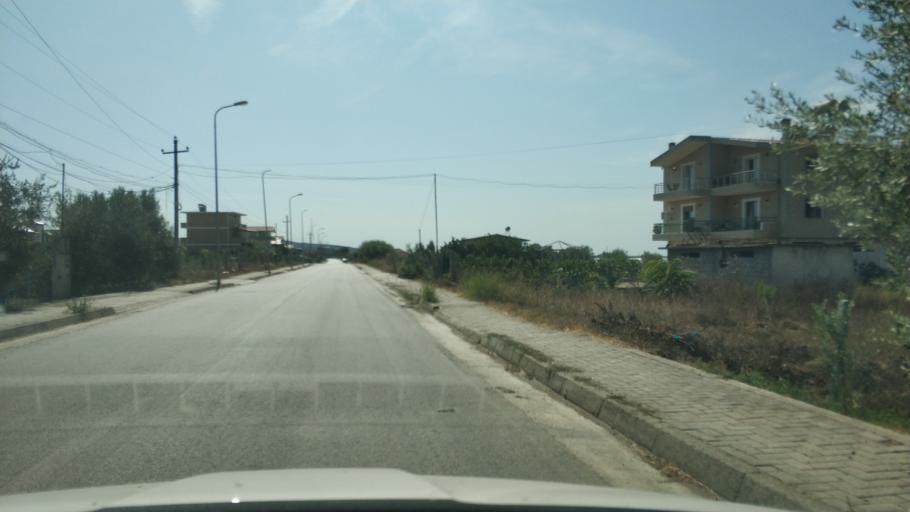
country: AL
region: Fier
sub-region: Rrethi i Lushnjes
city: Divjake
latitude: 40.9836
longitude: 19.5345
